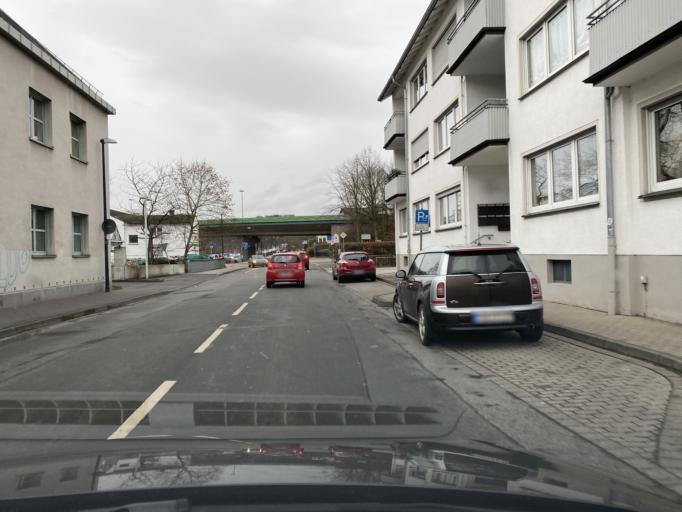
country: DE
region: North Rhine-Westphalia
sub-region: Regierungsbezirk Arnsberg
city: Meschede
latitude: 51.3499
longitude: 8.2807
